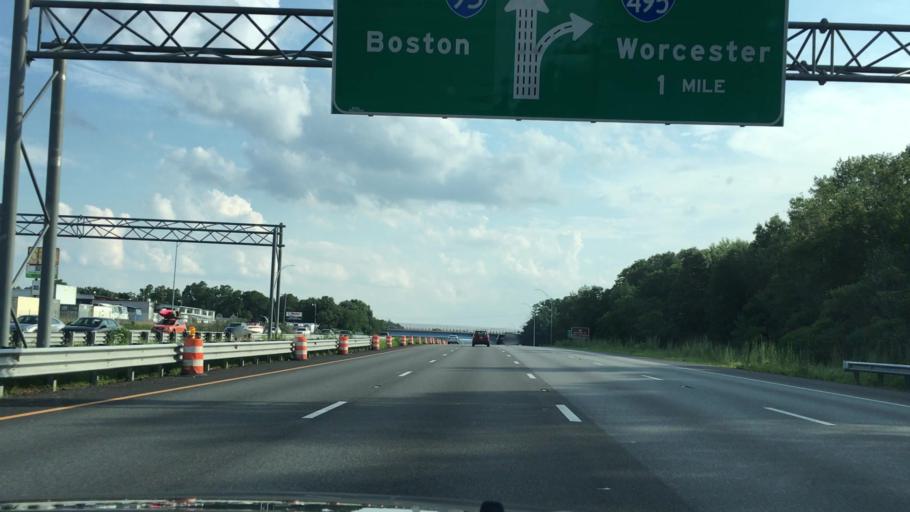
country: US
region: New Hampshire
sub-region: Rockingham County
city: Seabrook
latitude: 42.8715
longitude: -70.8887
